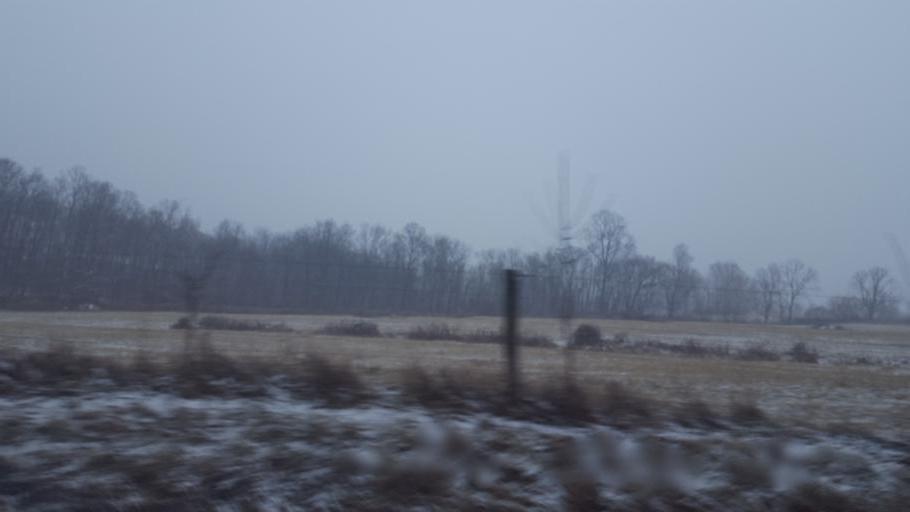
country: US
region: Ohio
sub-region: Coshocton County
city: West Lafayette
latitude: 40.3410
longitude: -81.7774
